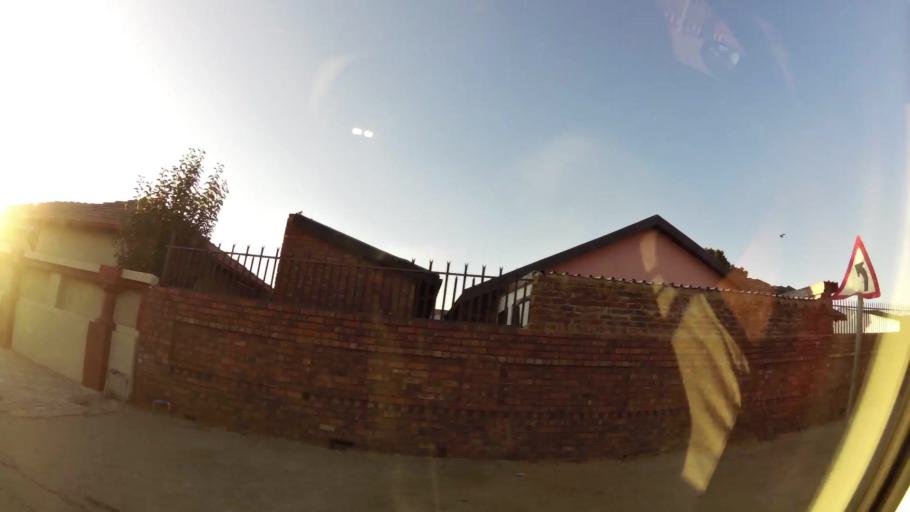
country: ZA
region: Gauteng
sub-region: City of Tshwane Metropolitan Municipality
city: Cullinan
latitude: -25.7278
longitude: 28.3969
